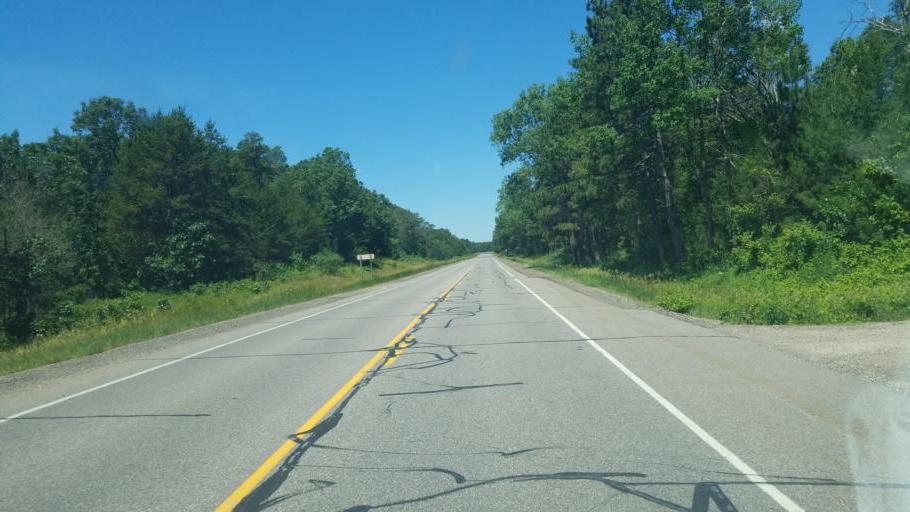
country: US
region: Wisconsin
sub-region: Adams County
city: Friendship
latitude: 44.0406
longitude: -89.9600
